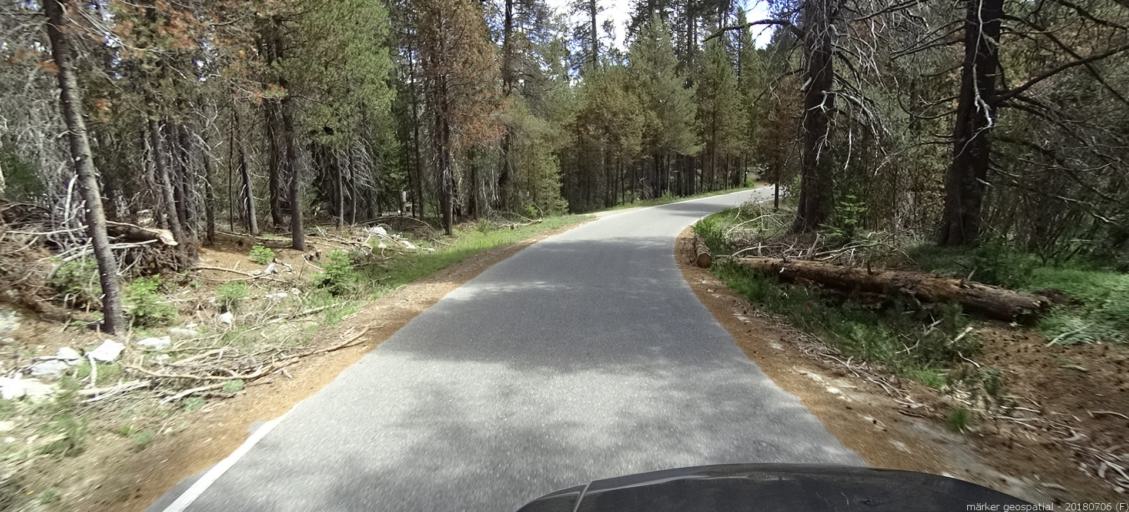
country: US
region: California
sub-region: Madera County
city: Oakhurst
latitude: 37.4479
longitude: -119.4533
